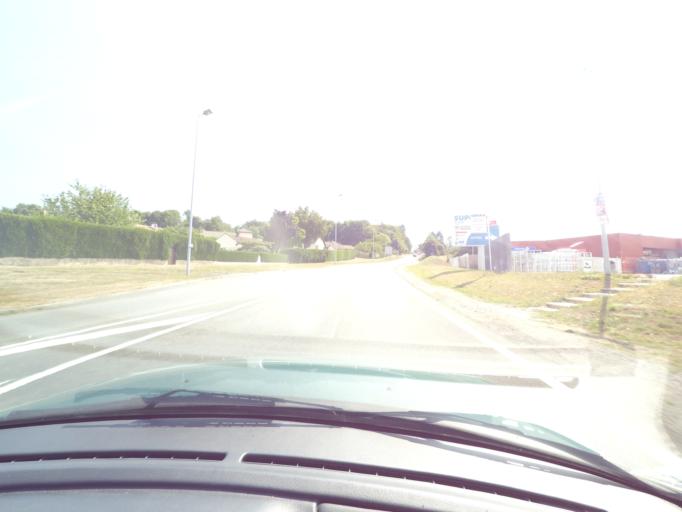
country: FR
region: Limousin
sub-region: Departement de la Haute-Vienne
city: Feytiat
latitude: 45.8135
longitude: 1.3218
